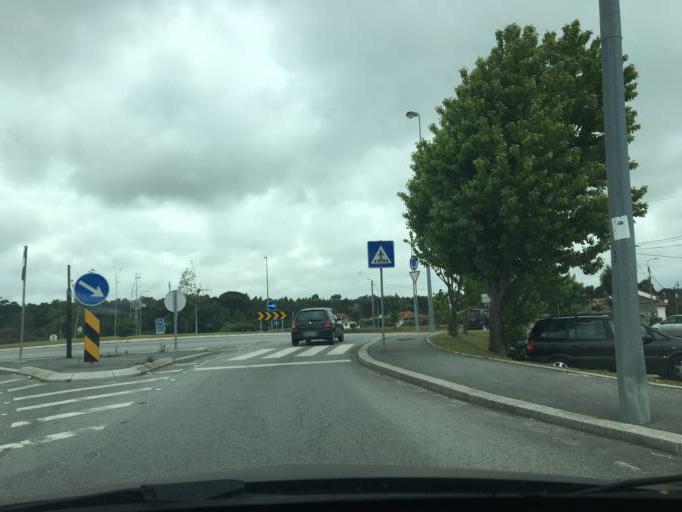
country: PT
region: Porto
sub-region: Matosinhos
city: Santa Cruz do Bispo
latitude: 41.2206
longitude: -8.6710
